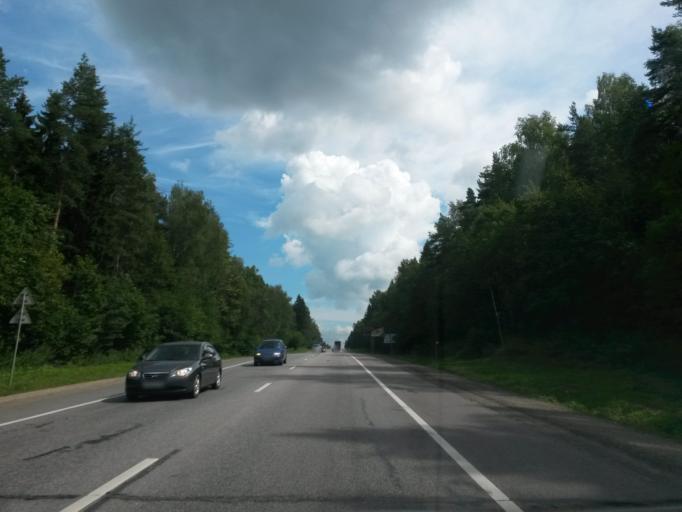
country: RU
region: Jaroslavl
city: Pereslavl'-Zalesskiy
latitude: 56.6946
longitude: 38.7652
